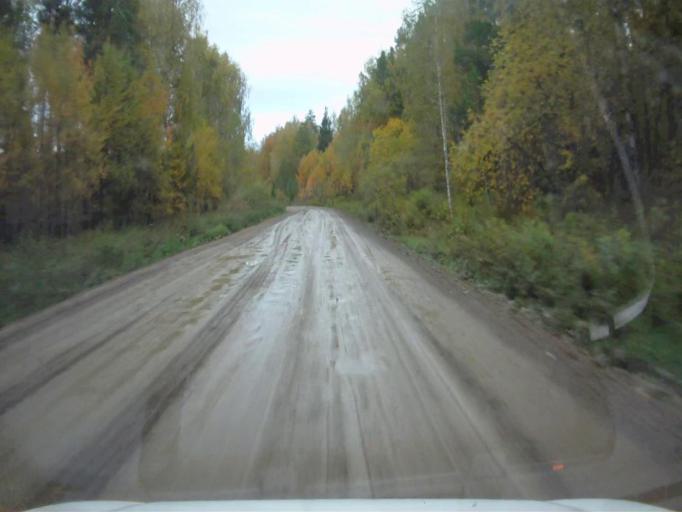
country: RU
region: Chelyabinsk
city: Nyazepetrovsk
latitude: 56.1192
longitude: 59.3694
